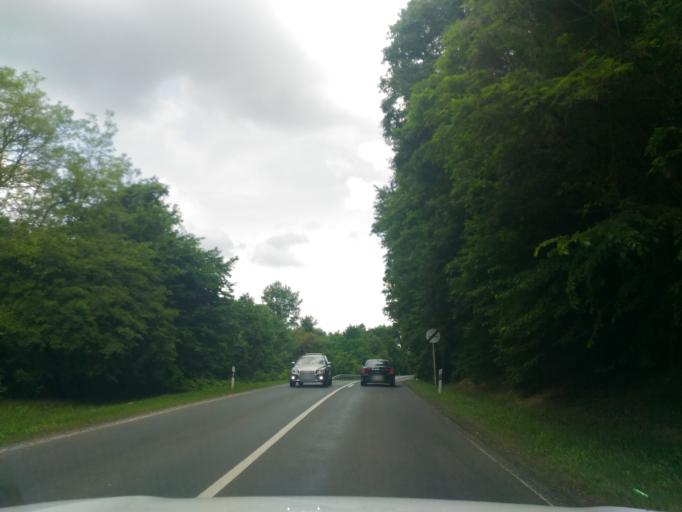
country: HU
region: Baranya
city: Komlo
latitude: 46.1768
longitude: 18.2104
